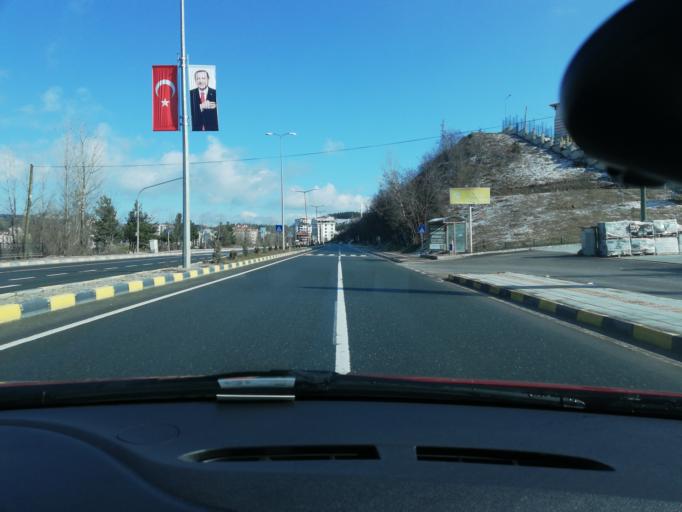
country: TR
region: Kastamonu
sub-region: Cide
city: Kastamonu
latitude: 41.3508
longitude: 33.7663
